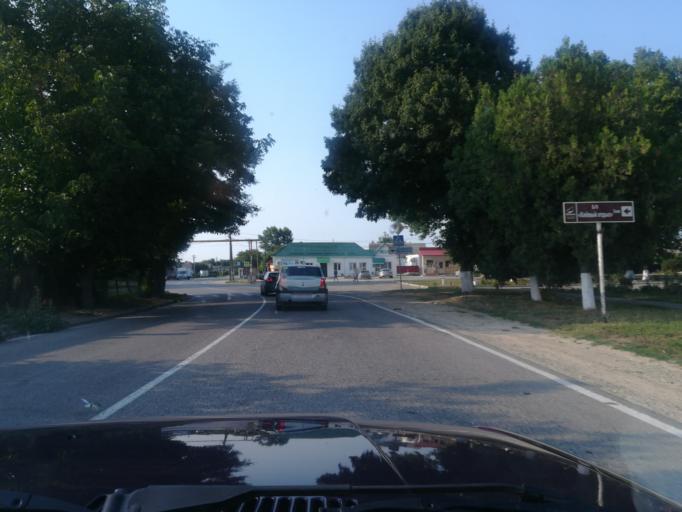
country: RU
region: Krasnodarskiy
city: Yurovka
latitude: 45.1136
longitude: 37.4224
